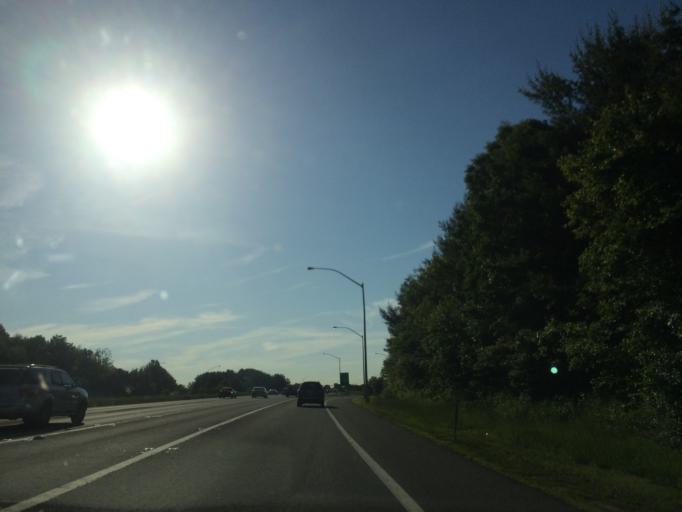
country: US
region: Maryland
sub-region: Howard County
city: Riverside
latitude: 39.1830
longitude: -76.8815
